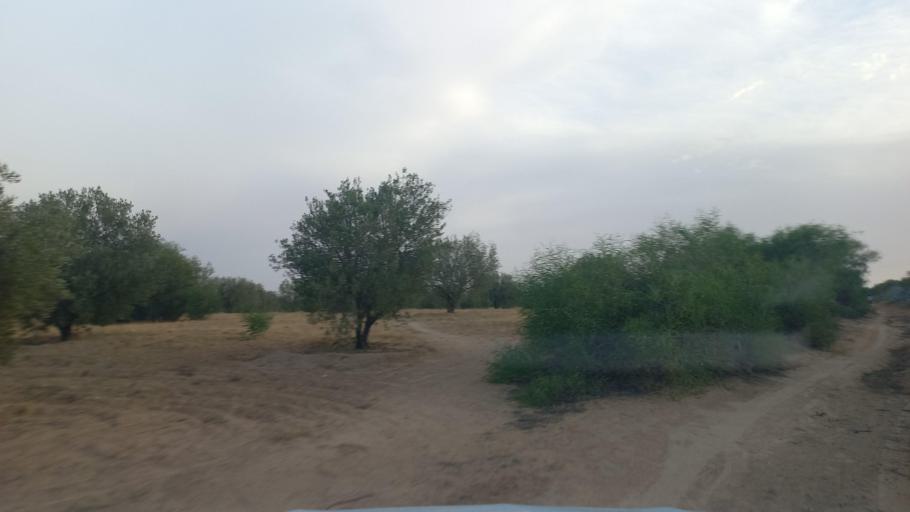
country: TN
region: Al Qasrayn
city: Kasserine
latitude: 35.2136
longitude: 9.0512
